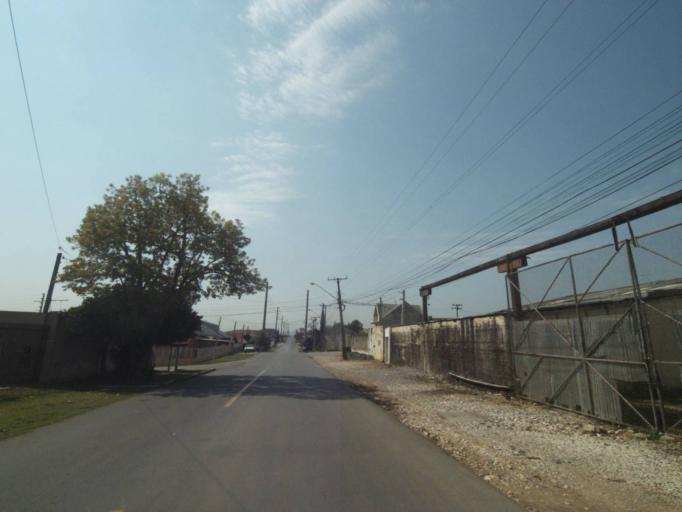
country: BR
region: Parana
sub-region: Sao Jose Dos Pinhais
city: Sao Jose dos Pinhais
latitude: -25.5117
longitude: -49.2848
